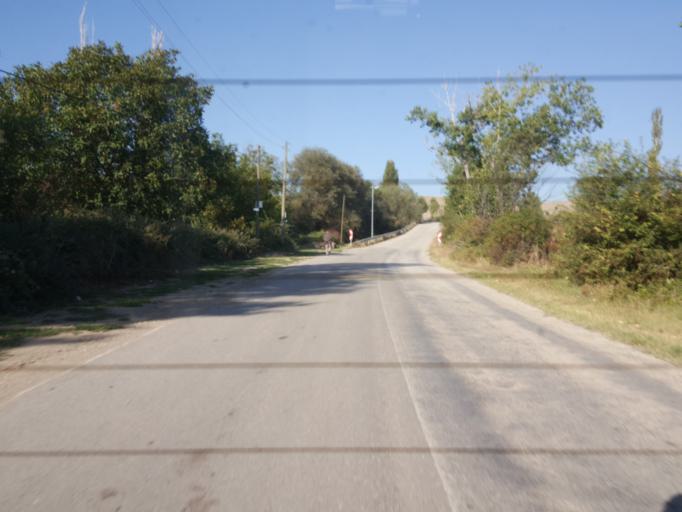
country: TR
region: Amasya
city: Saribugday
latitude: 40.7505
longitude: 35.4508
